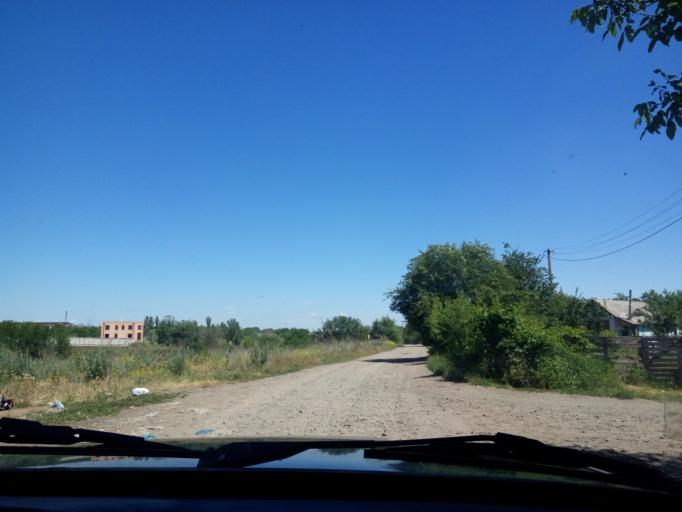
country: RU
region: Rostov
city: Bataysk
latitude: 47.0815
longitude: 39.7477
